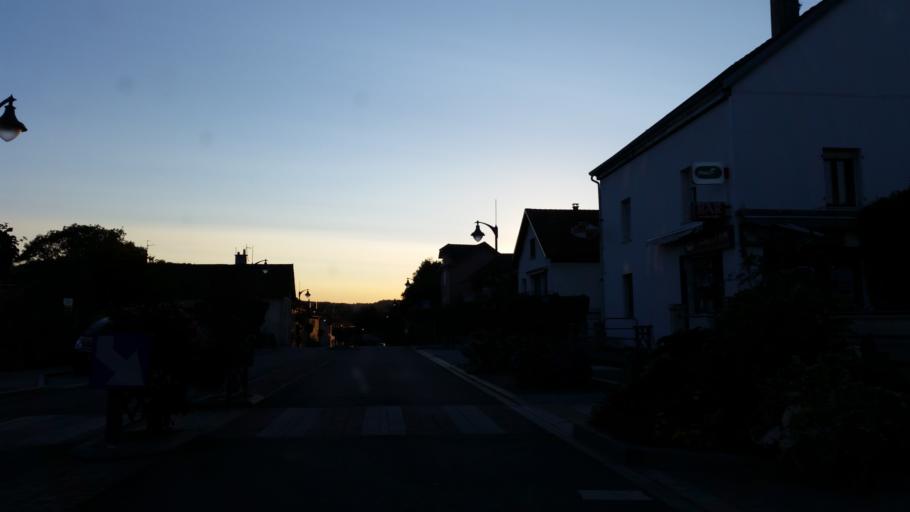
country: FR
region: Lorraine
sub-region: Departement des Vosges
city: Saint-Etienne-les-Remiremont
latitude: 48.0214
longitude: 6.6069
